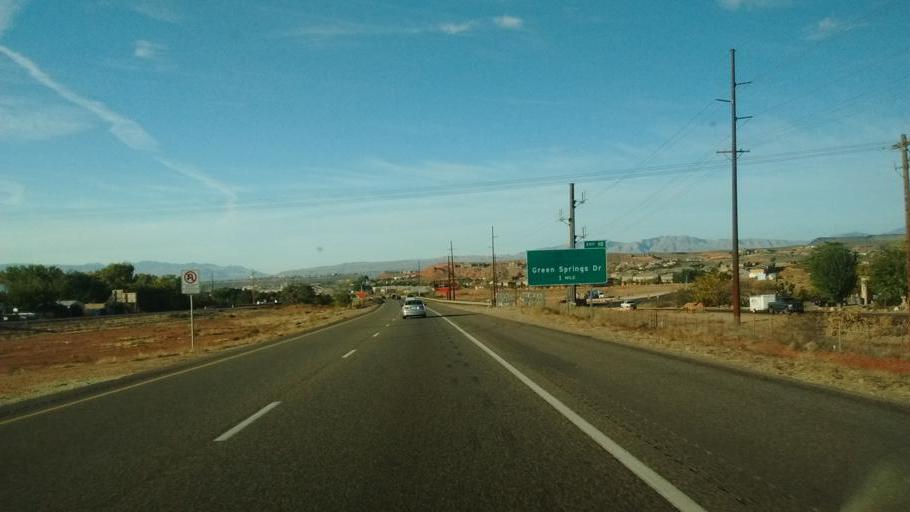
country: US
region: Utah
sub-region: Washington County
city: Washington
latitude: 37.1408
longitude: -113.5065
